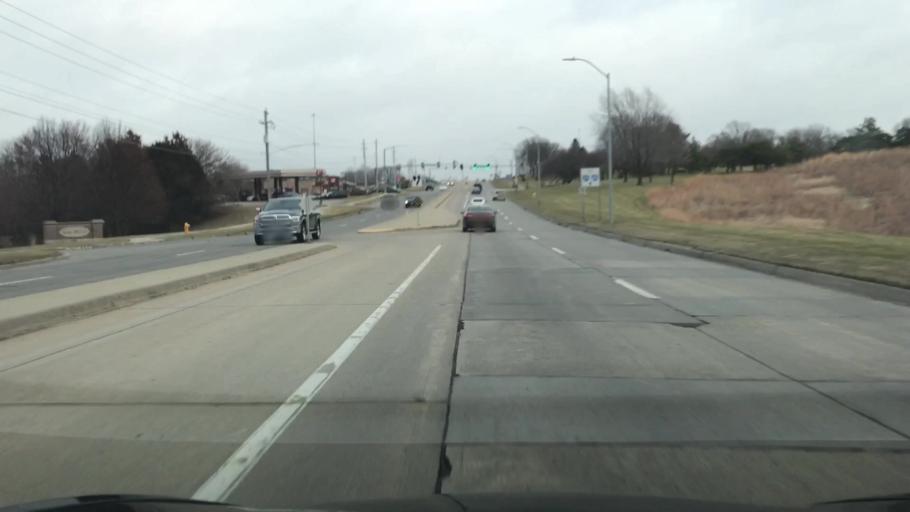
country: US
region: Iowa
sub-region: Polk County
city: Clive
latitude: 41.6004
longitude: -93.7844
